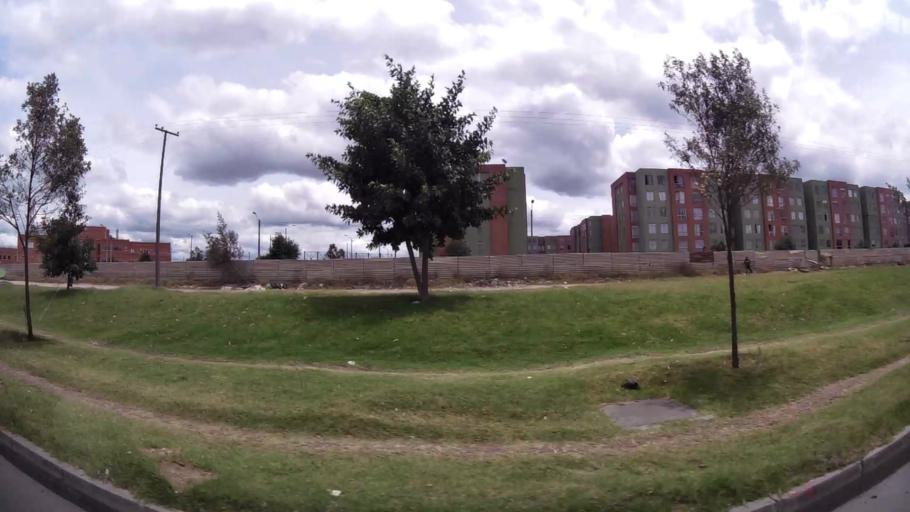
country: CO
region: Bogota D.C.
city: Bogota
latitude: 4.6501
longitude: -74.1485
